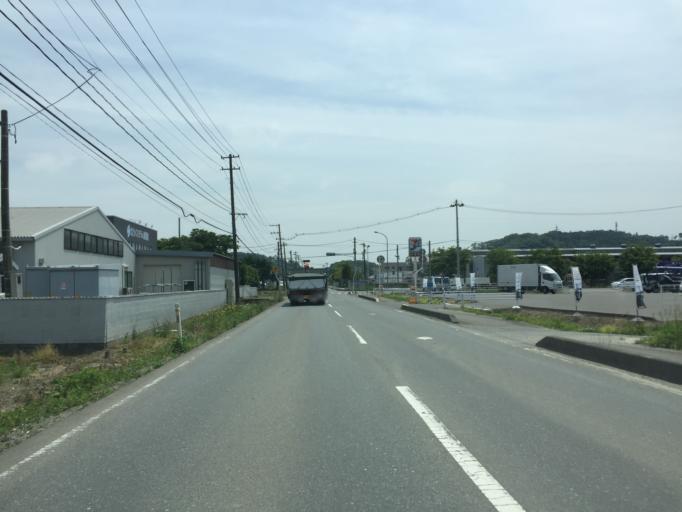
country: JP
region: Fukushima
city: Namie
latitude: 37.6543
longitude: 140.9314
